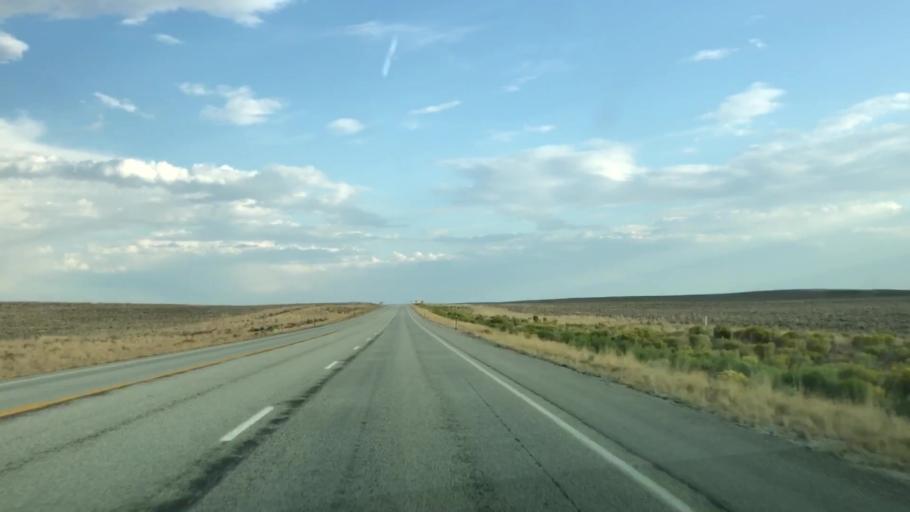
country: US
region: Wyoming
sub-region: Sweetwater County
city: North Rock Springs
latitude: 42.2701
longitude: -109.4785
